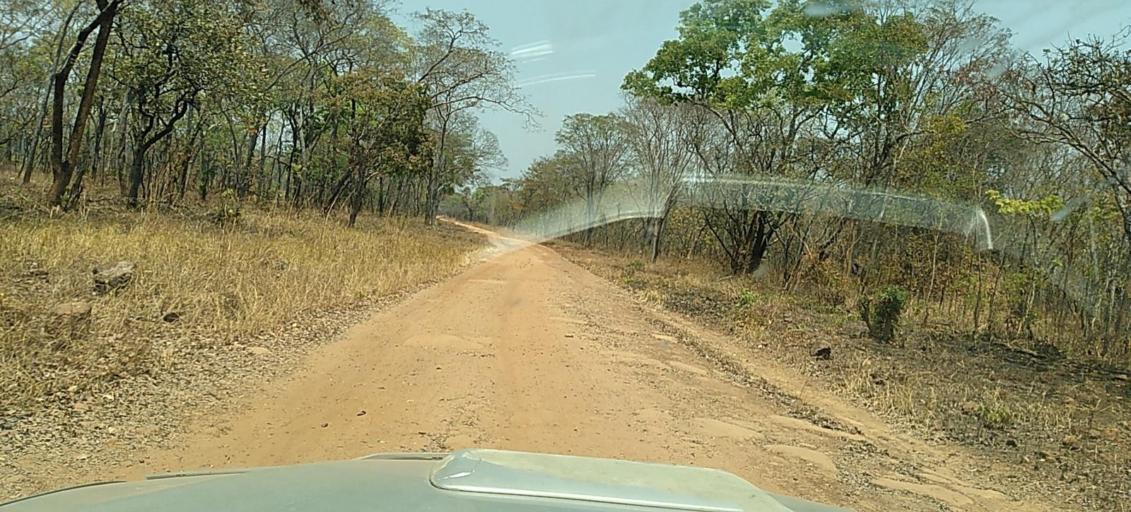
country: ZM
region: North-Western
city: Kasempa
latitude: -13.6117
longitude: 26.1965
